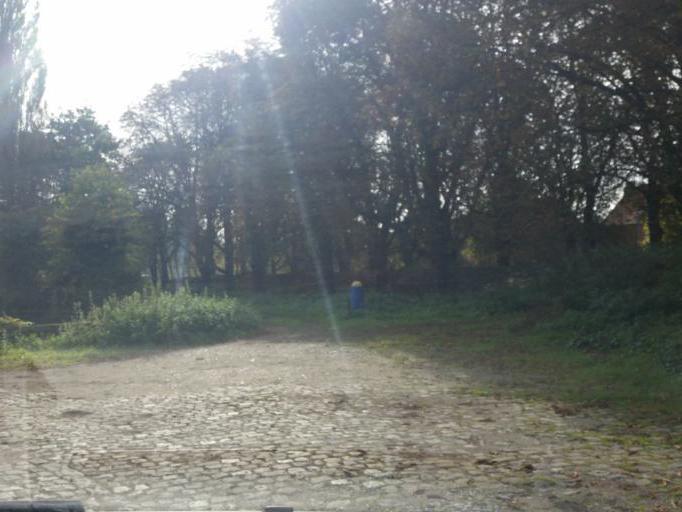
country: BE
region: Flanders
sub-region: Provincie Antwerpen
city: Borsbeek
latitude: 51.2034
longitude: 4.4899
